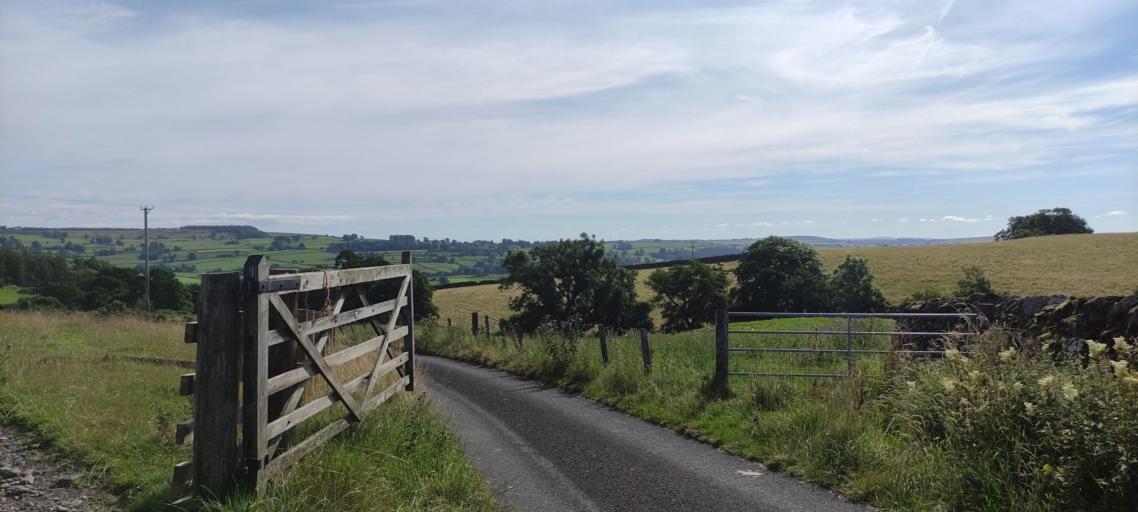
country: GB
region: England
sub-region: Cumbria
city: Penrith
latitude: 54.5481
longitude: -2.7613
